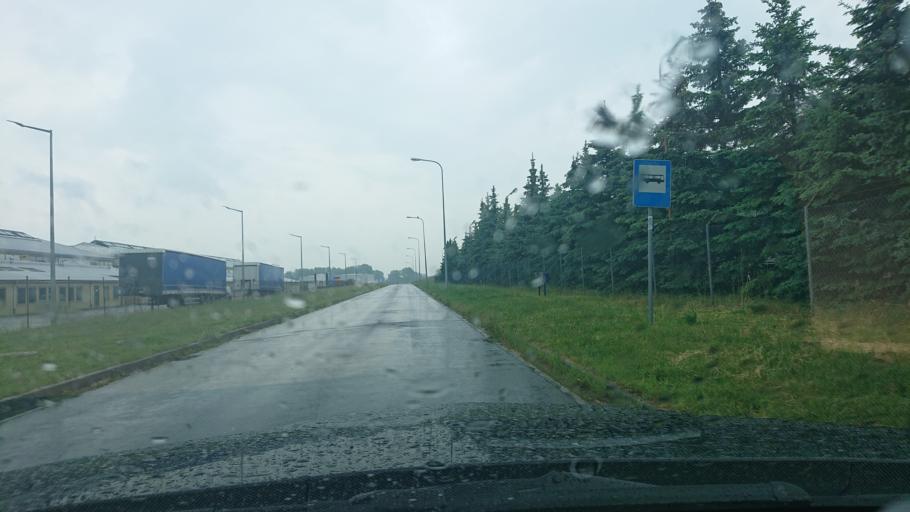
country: PL
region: Greater Poland Voivodeship
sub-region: Powiat gnieznienski
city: Gniezno
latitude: 52.5300
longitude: 17.6276
